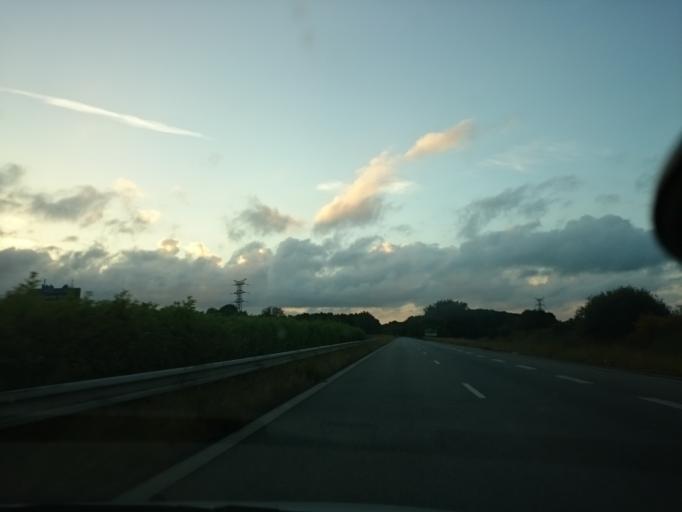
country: FR
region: Brittany
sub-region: Departement du Morbihan
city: Gestel
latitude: 47.8100
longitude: -3.4606
